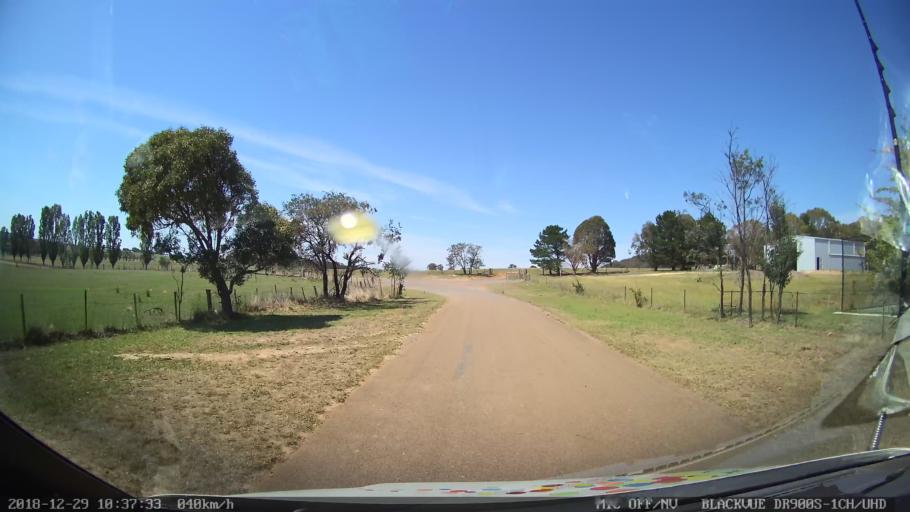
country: AU
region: New South Wales
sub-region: Yass Valley
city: Gundaroo
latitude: -34.9983
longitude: 149.4989
